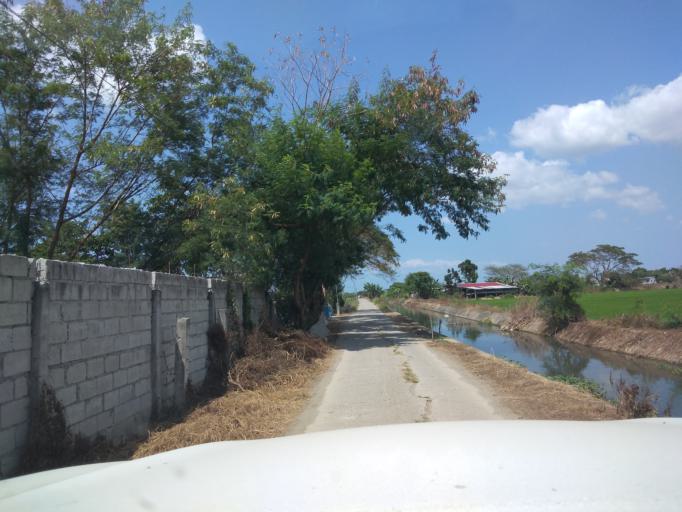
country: PH
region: Central Luzon
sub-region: Province of Pampanga
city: Bahay Pare
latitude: 15.0428
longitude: 120.8738
